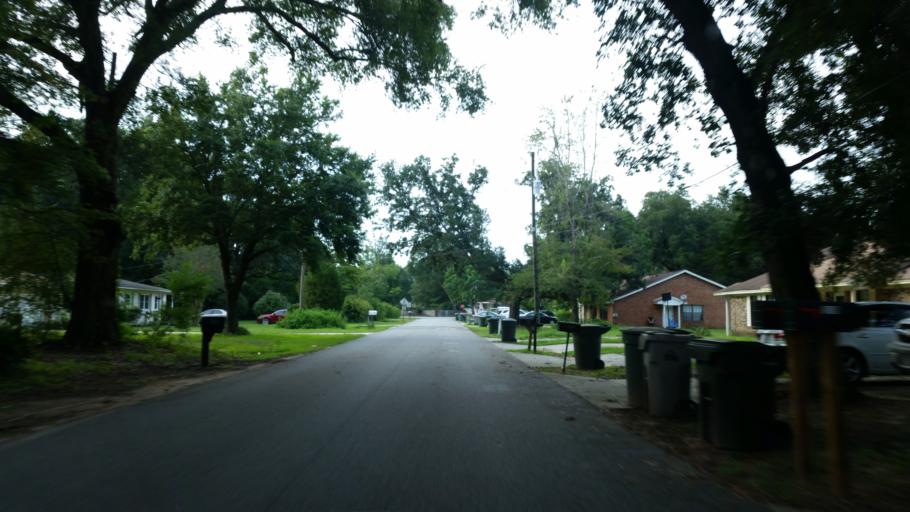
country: US
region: Florida
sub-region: Escambia County
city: Ferry Pass
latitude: 30.5156
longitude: -87.2084
